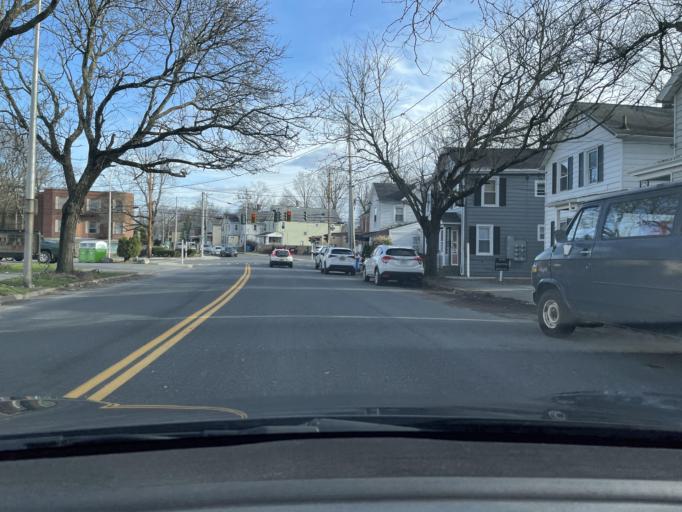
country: US
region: New York
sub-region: Ulster County
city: Kingston
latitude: 41.9337
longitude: -74.0245
